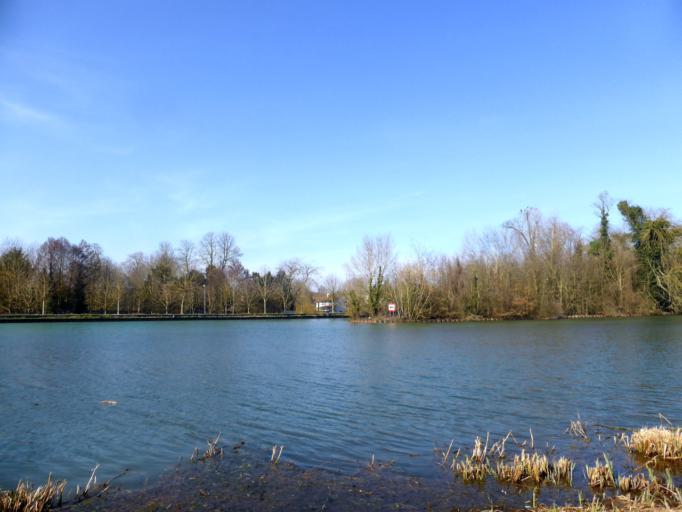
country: FR
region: Champagne-Ardenne
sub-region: Departement de la Marne
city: Chalons-en-Champagne
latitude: 48.9516
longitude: 4.3580
